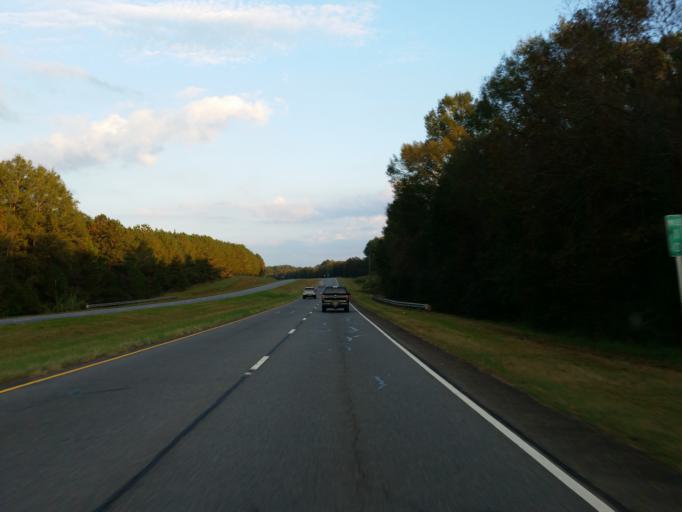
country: US
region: Georgia
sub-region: Houston County
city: Perry
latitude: 32.4144
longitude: -83.6838
